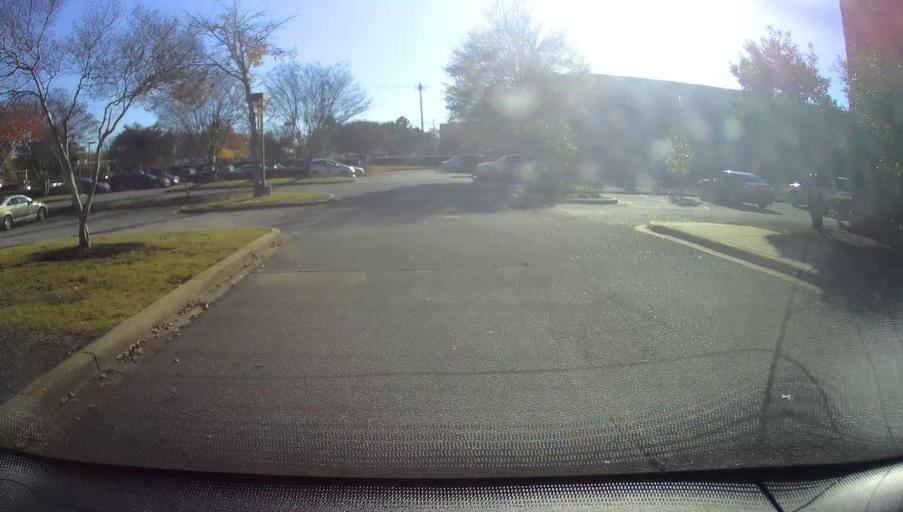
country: US
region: Tennessee
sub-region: Shelby County
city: Germantown
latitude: 35.1141
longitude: -89.8028
